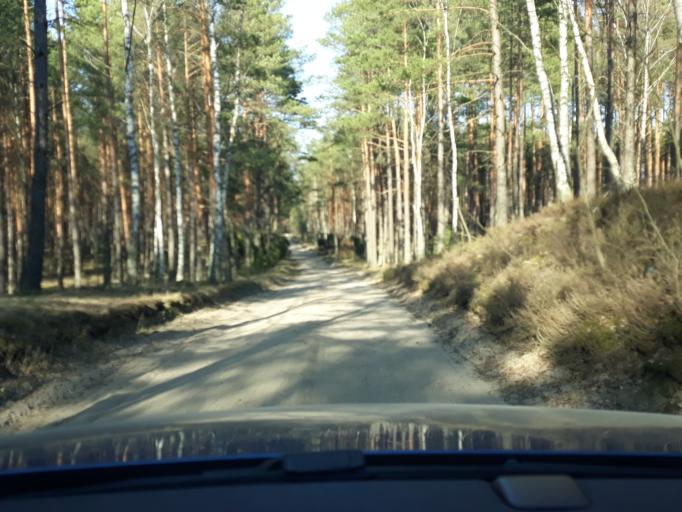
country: PL
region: Pomeranian Voivodeship
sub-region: Powiat bytowski
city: Lipnica
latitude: 53.9079
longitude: 17.4256
